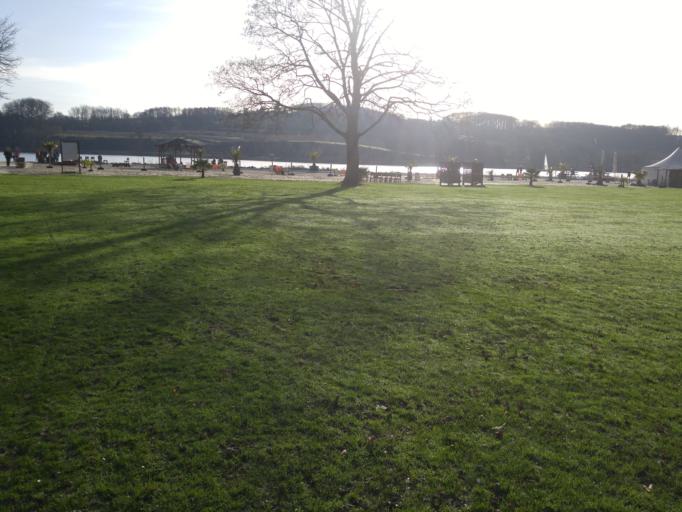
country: DE
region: North Rhine-Westphalia
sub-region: Regierungsbezirk Dusseldorf
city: Essen
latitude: 51.4073
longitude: 7.0205
